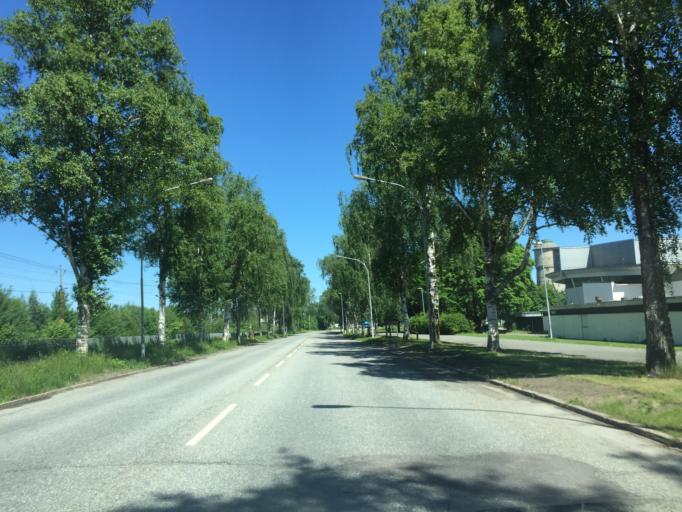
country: SE
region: OErebro
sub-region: Orebro Kommun
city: Orebro
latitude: 59.2600
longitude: 15.1908
